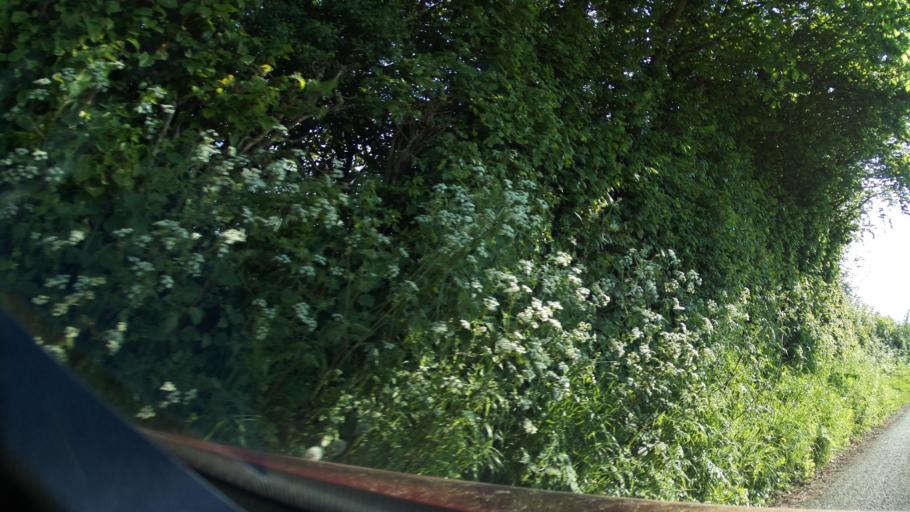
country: GB
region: England
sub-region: Wiltshire
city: Biddestone
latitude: 51.4931
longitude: -2.1957
